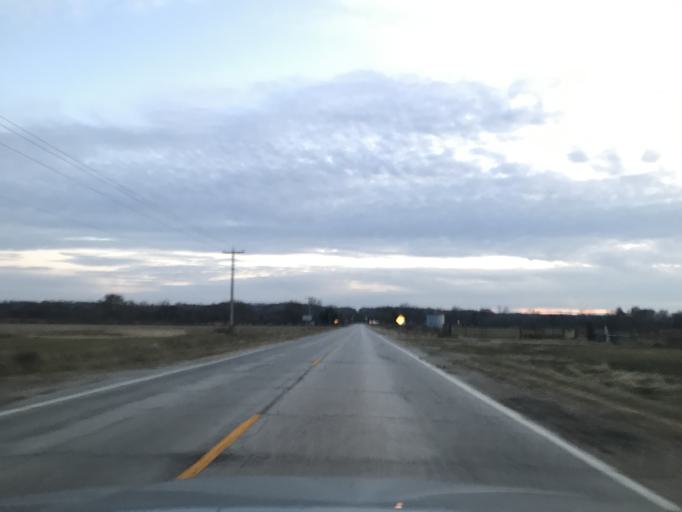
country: US
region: Iowa
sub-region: Des Moines County
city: Burlington
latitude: 40.6890
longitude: -91.0702
